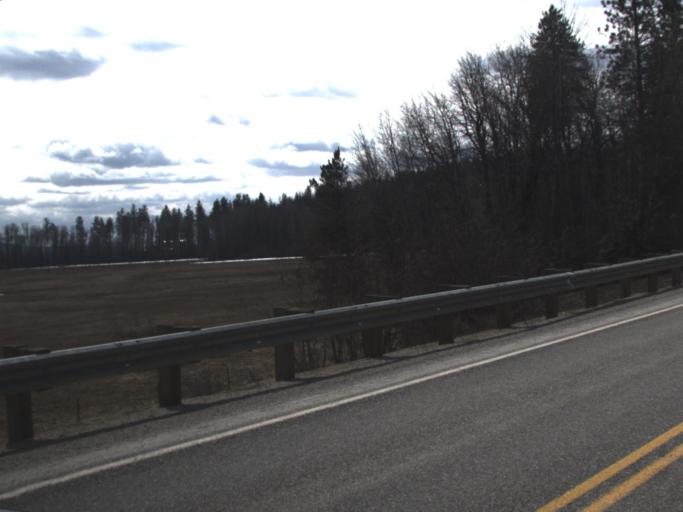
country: US
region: Washington
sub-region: Pend Oreille County
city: Newport
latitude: 48.4226
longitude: -117.3178
